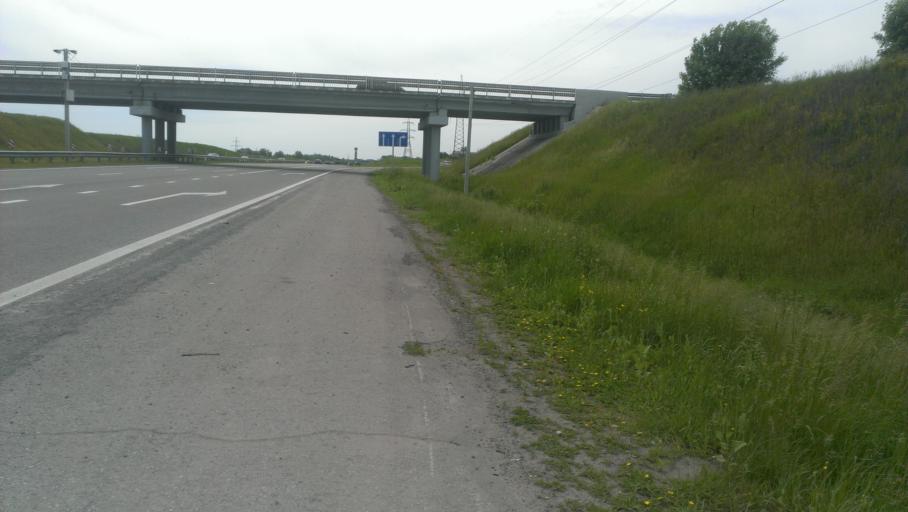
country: RU
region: Altai Krai
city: Sannikovo
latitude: 53.3413
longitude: 83.9368
